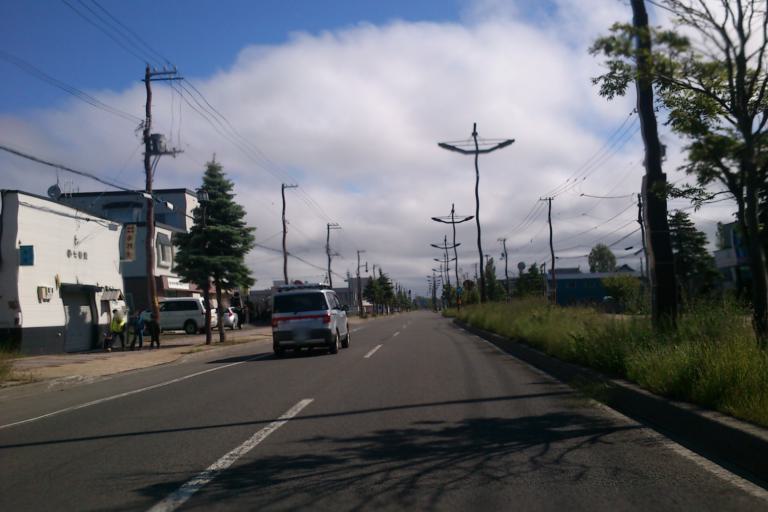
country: JP
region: Hokkaido
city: Ishikari
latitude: 43.1743
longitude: 141.3170
